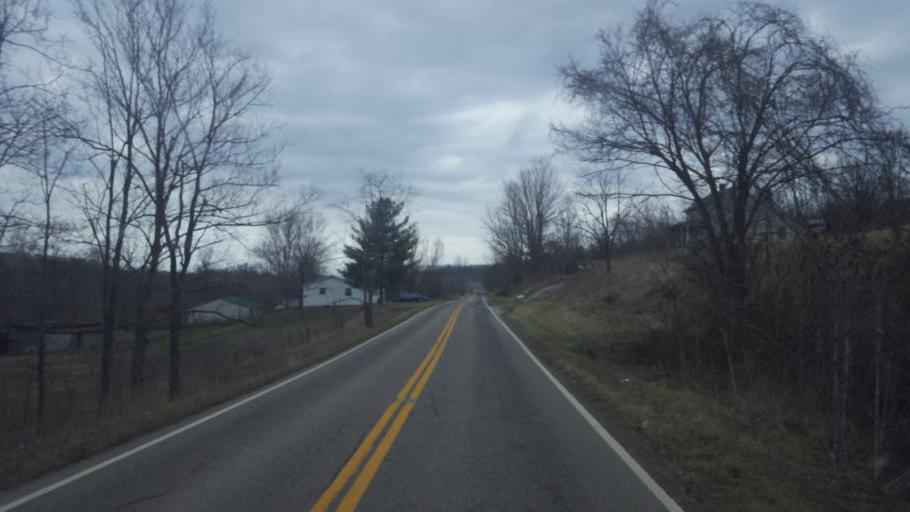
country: US
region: Ohio
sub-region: Gallia County
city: Gallipolis
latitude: 38.7345
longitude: -82.3692
